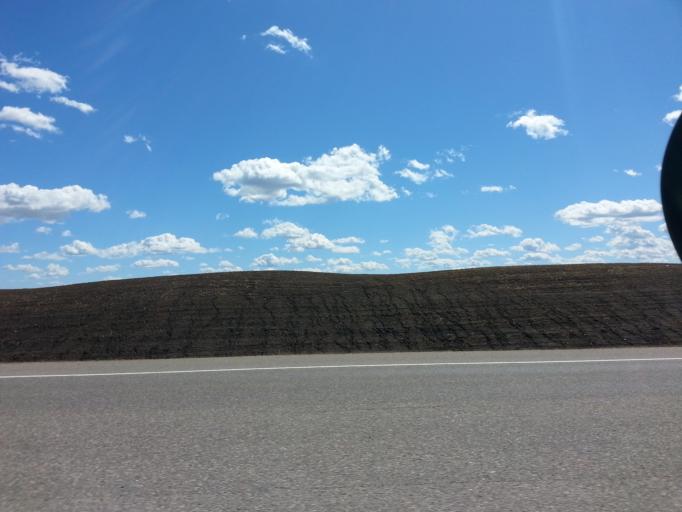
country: US
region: Minnesota
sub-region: Dakota County
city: Rosemount
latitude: 44.7173
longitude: -93.1186
